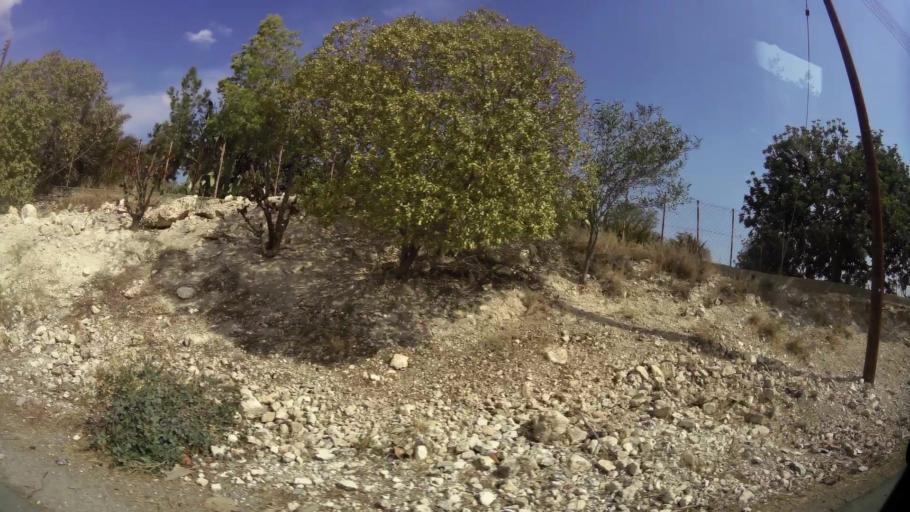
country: CY
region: Larnaka
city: Aradippou
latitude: 34.9632
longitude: 33.5658
